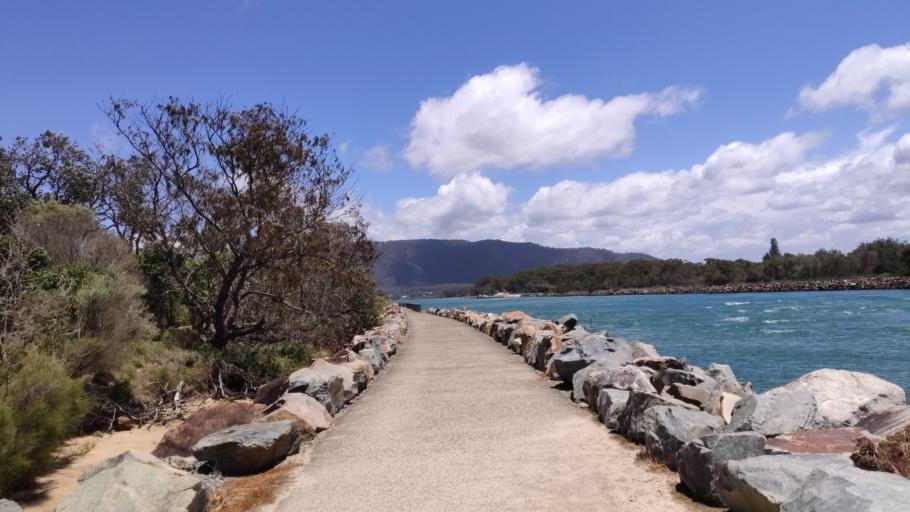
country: AU
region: New South Wales
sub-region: Port Macquarie-Hastings
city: North Haven
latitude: -31.6376
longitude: 152.8330
